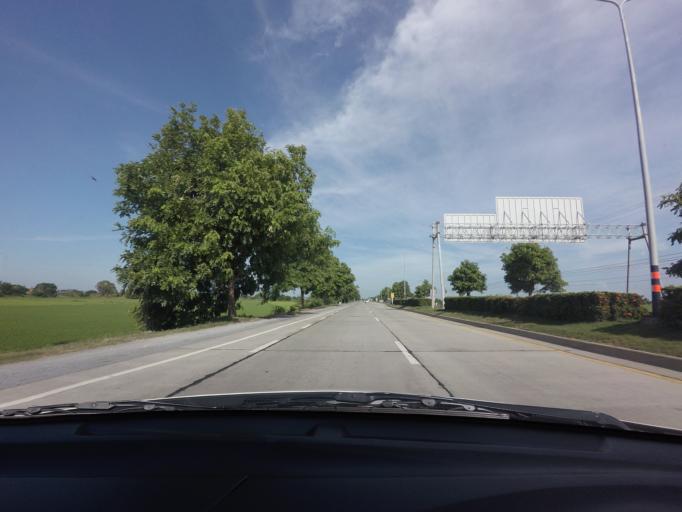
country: TH
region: Suphan Buri
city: Suphan Buri
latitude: 14.4617
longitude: 100.0511
